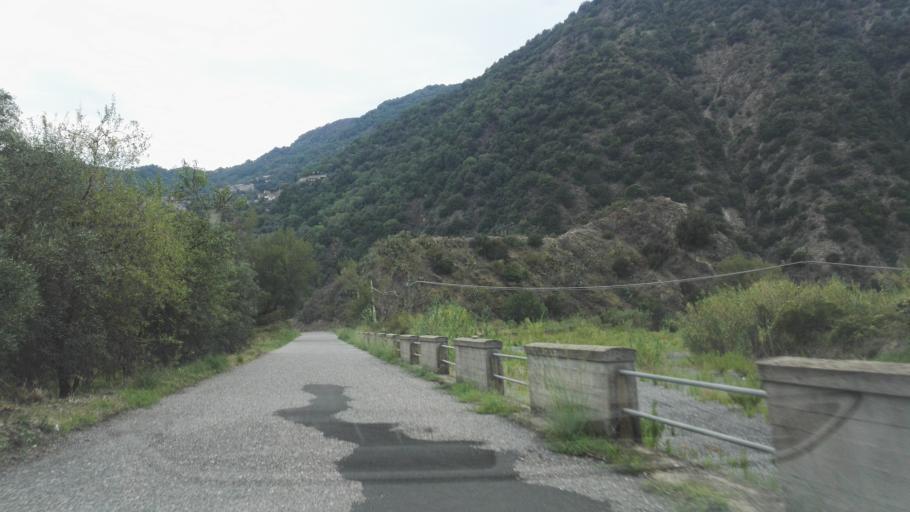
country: IT
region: Calabria
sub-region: Provincia di Reggio Calabria
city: Caulonia
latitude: 38.4215
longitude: 16.3795
